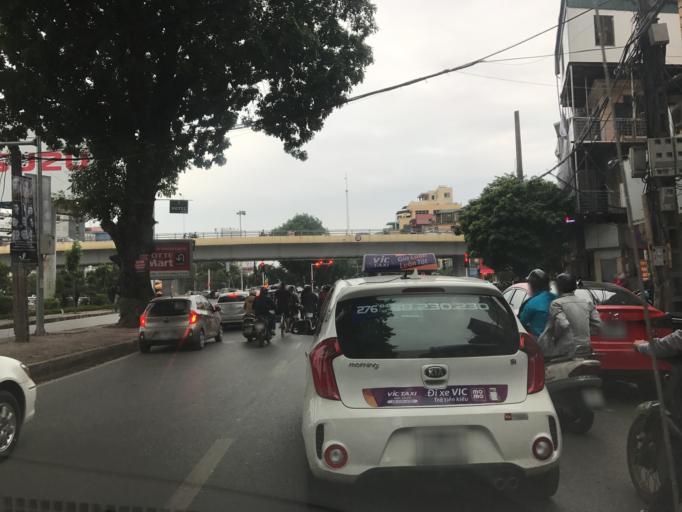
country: VN
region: Ha Noi
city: Cau Giay
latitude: 21.0149
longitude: 105.8057
